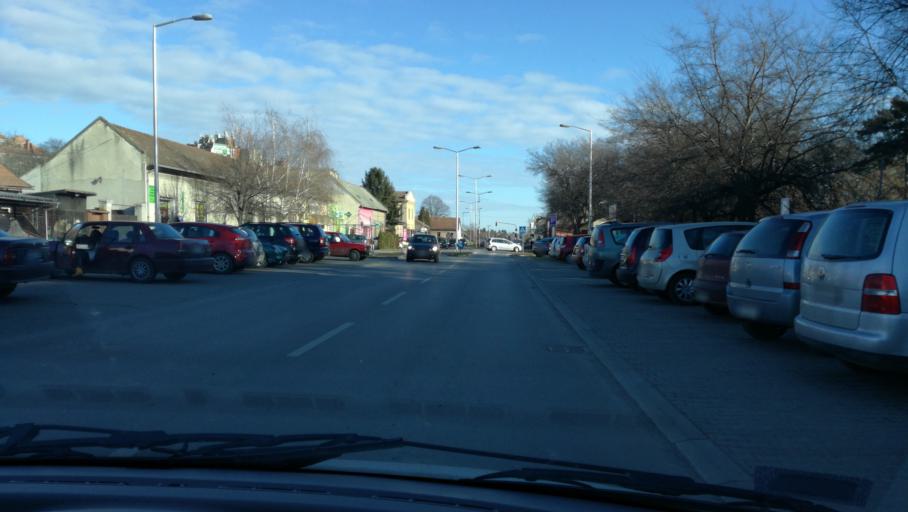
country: RS
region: Autonomna Pokrajina Vojvodina
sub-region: Severnobacki Okrug
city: Subotica
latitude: 46.0820
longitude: 19.6711
